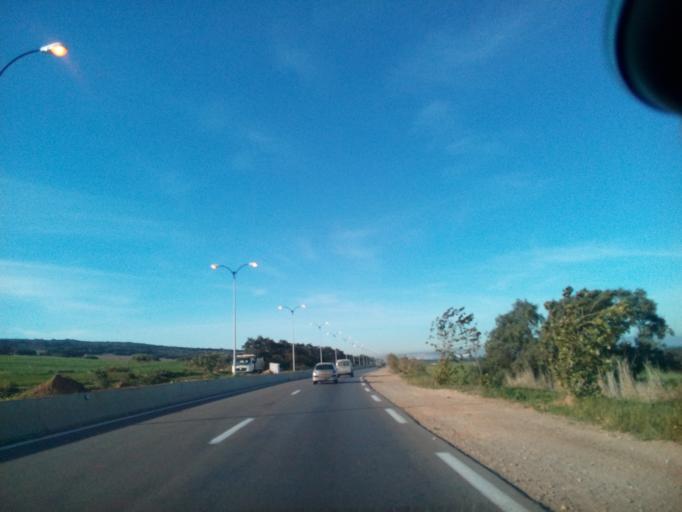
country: DZ
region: Mostaganem
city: Mostaganem
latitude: 35.8053
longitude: -0.0500
